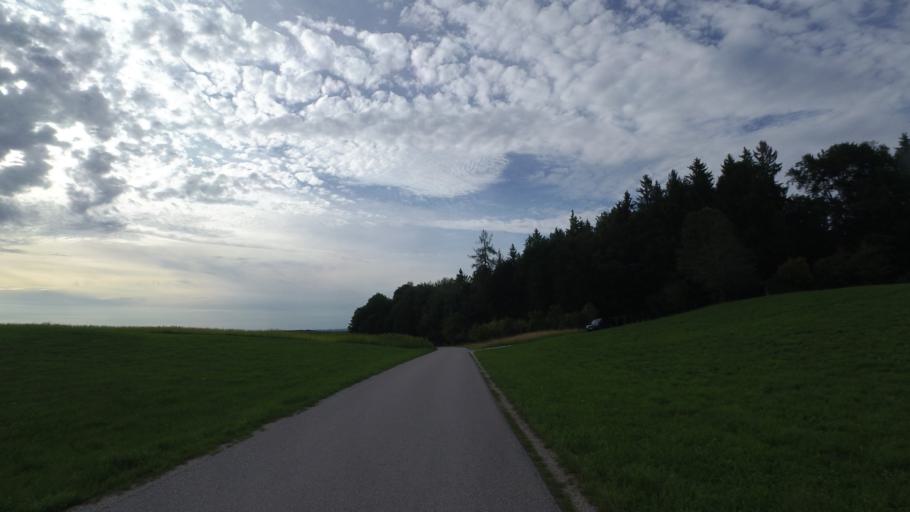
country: DE
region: Bavaria
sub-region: Upper Bavaria
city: Vachendorf
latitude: 47.8637
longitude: 12.6018
